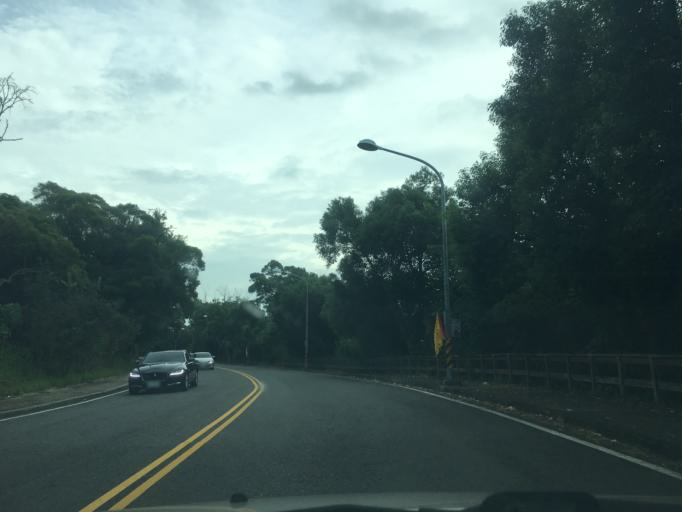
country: TW
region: Taiwan
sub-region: Changhua
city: Chang-hua
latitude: 24.0644
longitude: 120.5701
